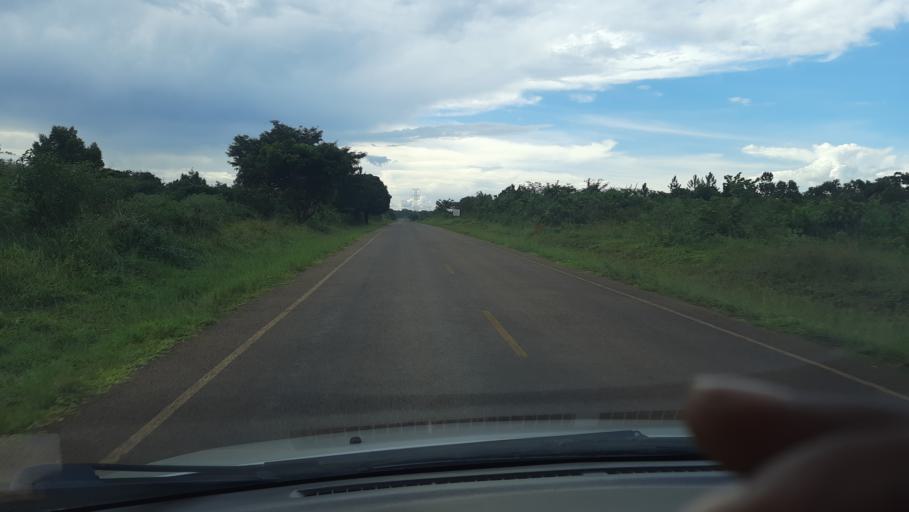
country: UG
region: Central Region
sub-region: Nakasongola District
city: Nakasongola
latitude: 1.3188
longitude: 32.4351
